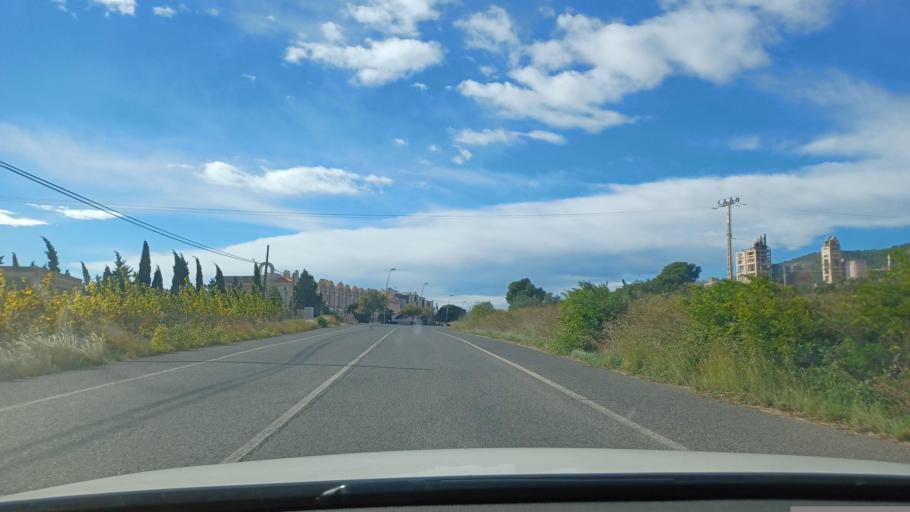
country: ES
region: Catalonia
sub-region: Provincia de Tarragona
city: Sant Carles de la Rapita
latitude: 40.5794
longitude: 0.5528
